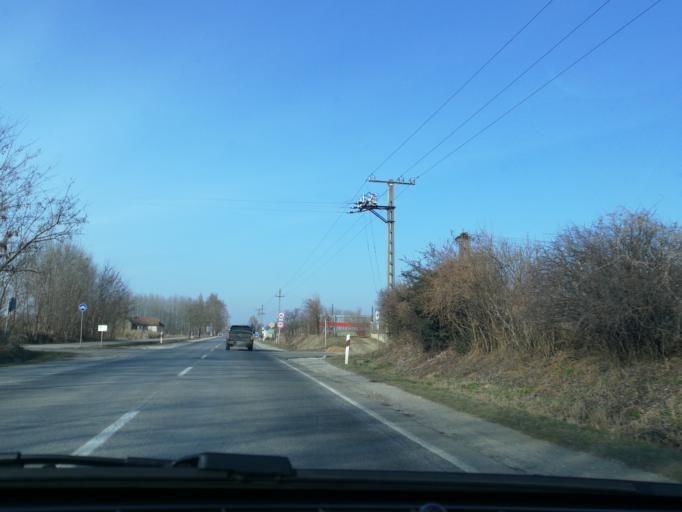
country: HU
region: Szabolcs-Szatmar-Bereg
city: Apagy
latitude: 47.9581
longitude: 21.9479
